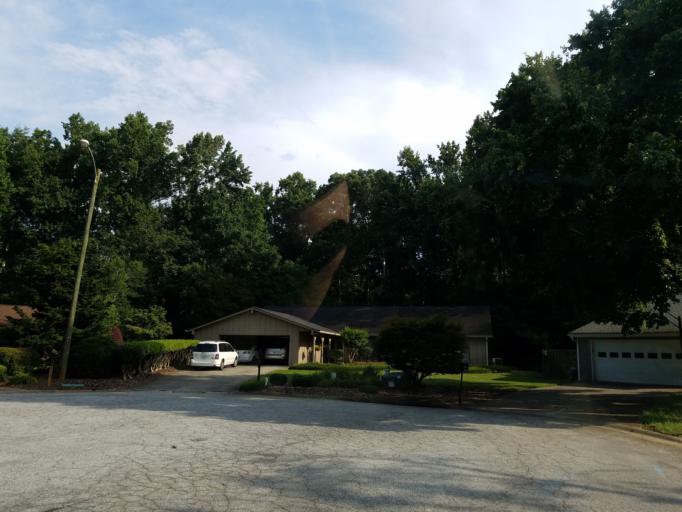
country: US
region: Georgia
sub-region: Fulton County
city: Sandy Springs
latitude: 33.9612
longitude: -84.4478
